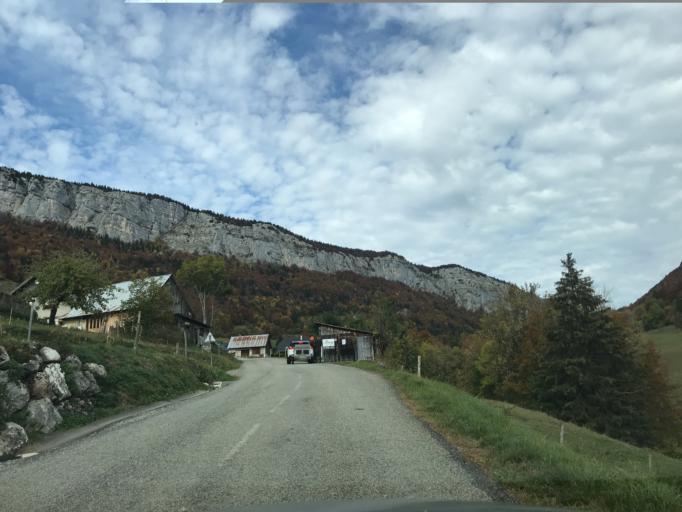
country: FR
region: Rhone-Alpes
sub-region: Departement de la Savoie
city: Vimines
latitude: 45.4629
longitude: 5.8658
